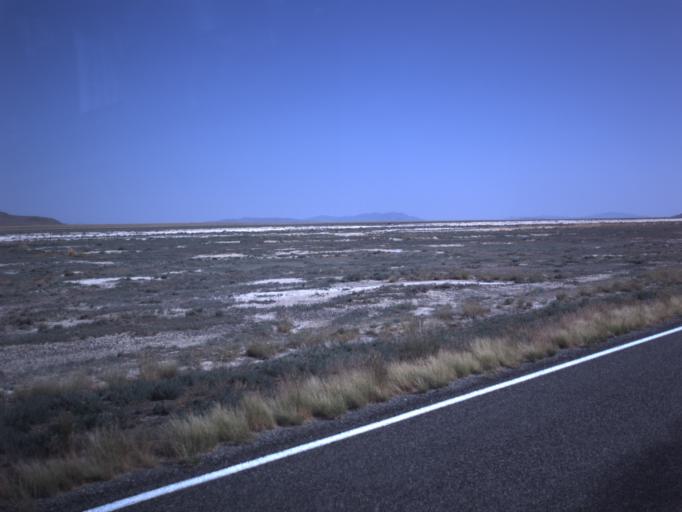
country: US
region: Utah
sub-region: Millard County
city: Delta
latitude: 39.0268
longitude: -112.7768
